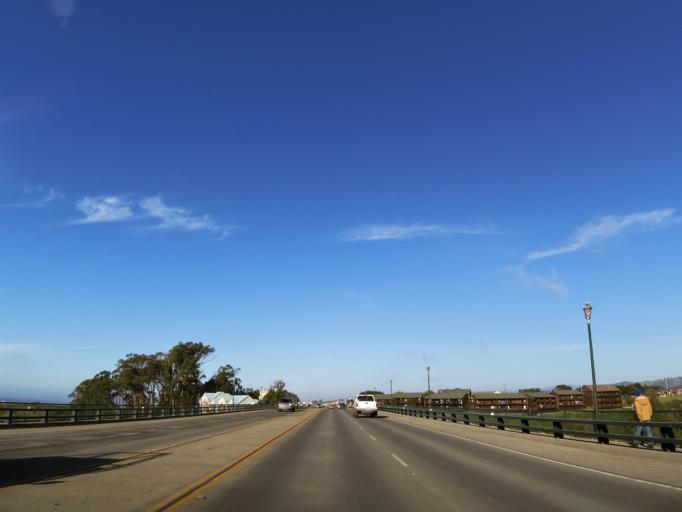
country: US
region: California
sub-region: Mendocino County
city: Fort Bragg
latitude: 39.4266
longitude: -123.8070
